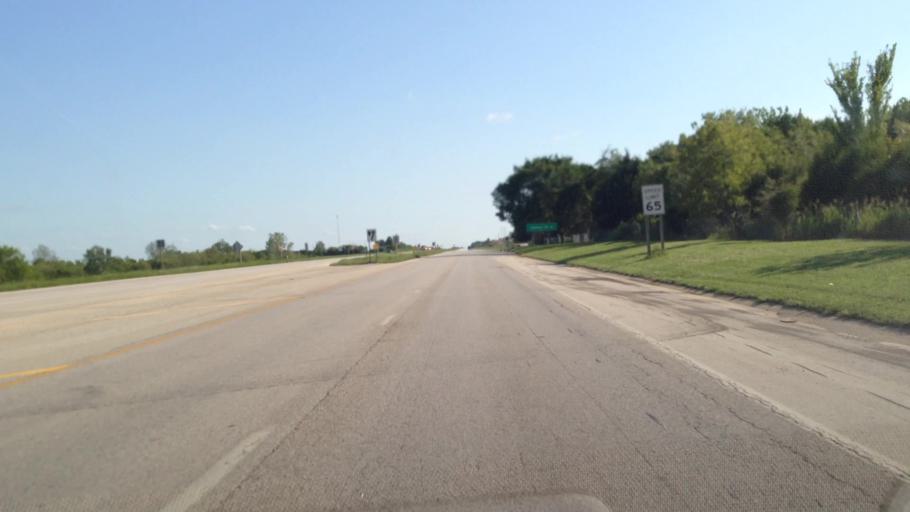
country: US
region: Kansas
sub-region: Bourbon County
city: Fort Scott
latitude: 37.8041
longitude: -94.7052
